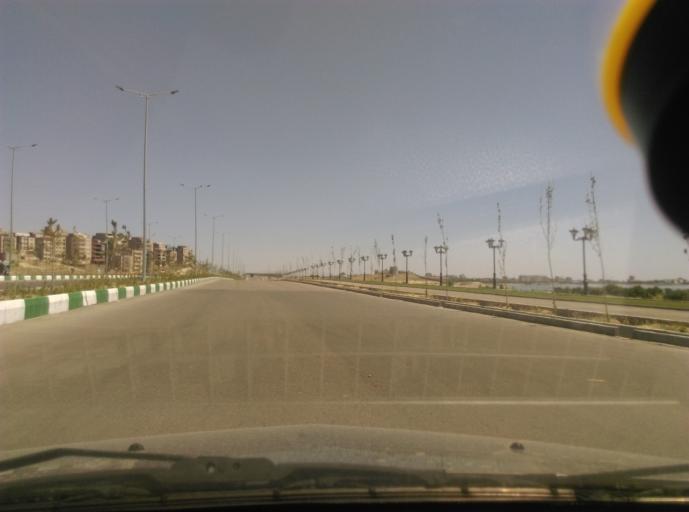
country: IR
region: Ardabil
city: Ardabil
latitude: 38.2082
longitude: 48.2662
